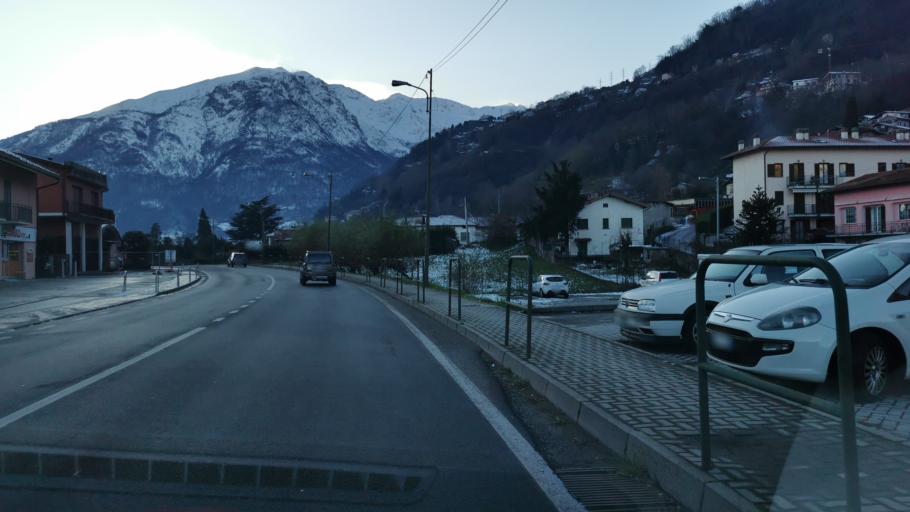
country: IT
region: Lombardy
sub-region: Provincia di Como
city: Consiglio di Rumo
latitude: 46.1410
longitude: 9.2926
